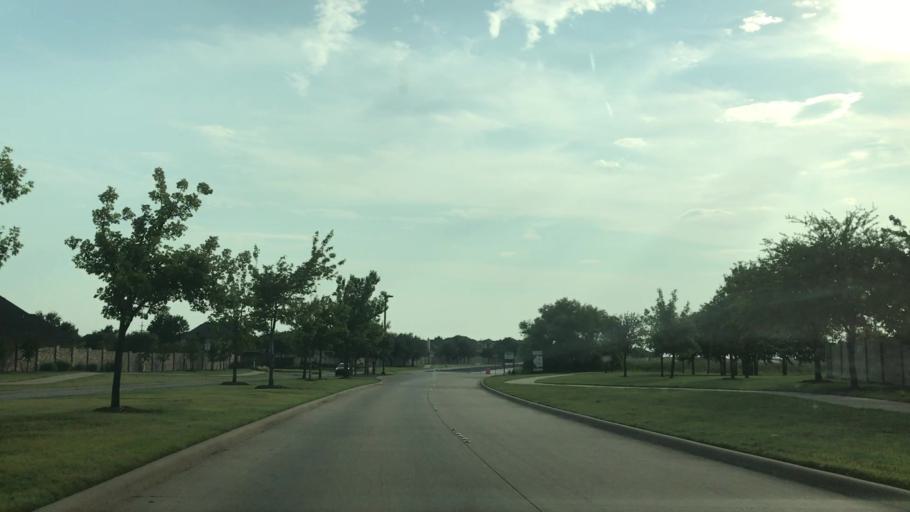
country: US
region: Texas
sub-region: Rockwall County
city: Fate
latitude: 32.9416
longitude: -96.3930
